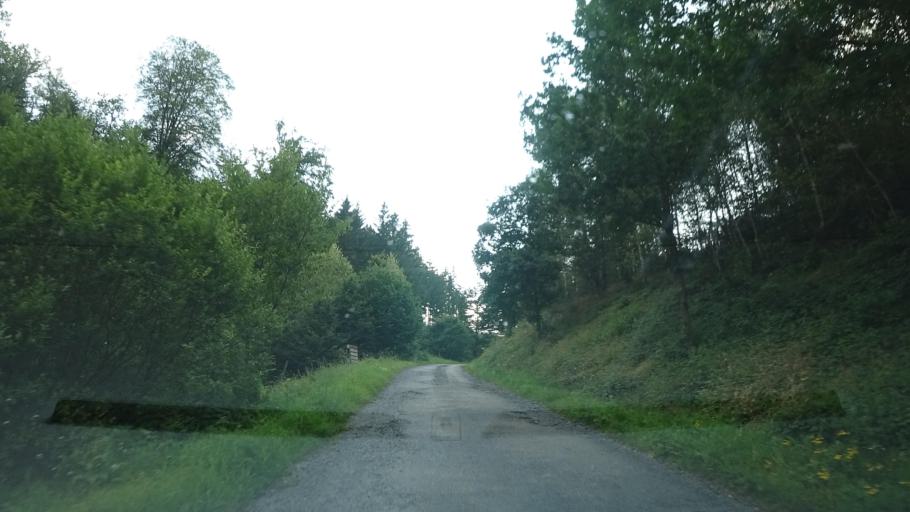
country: BE
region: Wallonia
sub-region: Province du Luxembourg
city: Herbeumont
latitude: 49.7827
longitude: 5.2559
